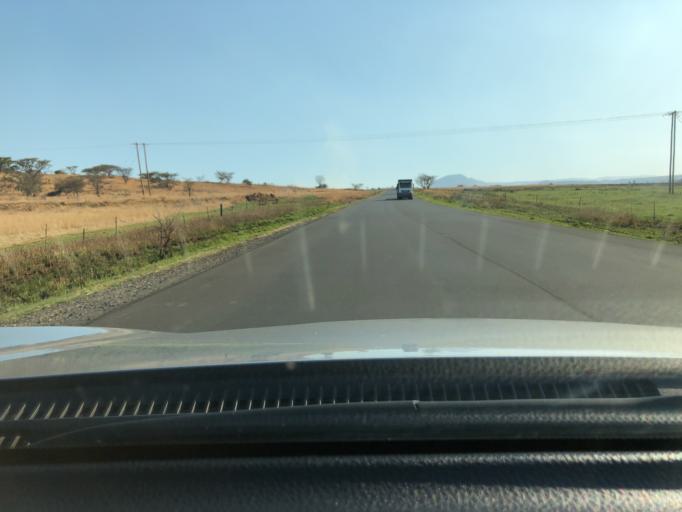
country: ZA
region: KwaZulu-Natal
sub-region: uThukela District Municipality
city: Ekuvukeni
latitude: -28.3622
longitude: 30.0063
